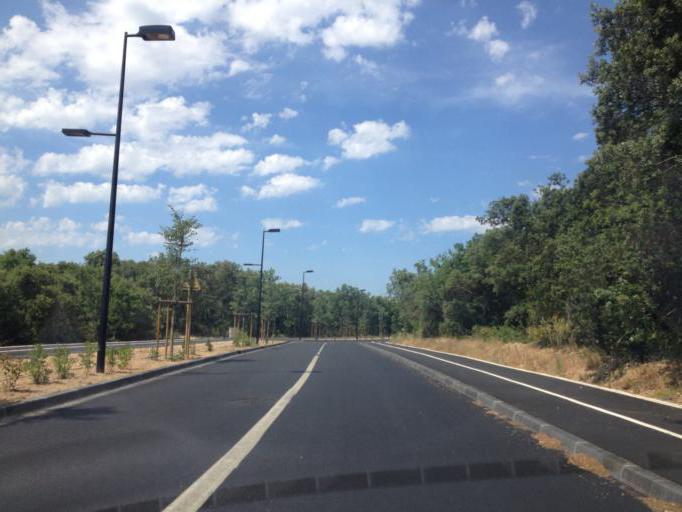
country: FR
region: Provence-Alpes-Cote d'Azur
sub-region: Departement du Vaucluse
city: Orange
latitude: 44.1151
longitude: 4.8242
